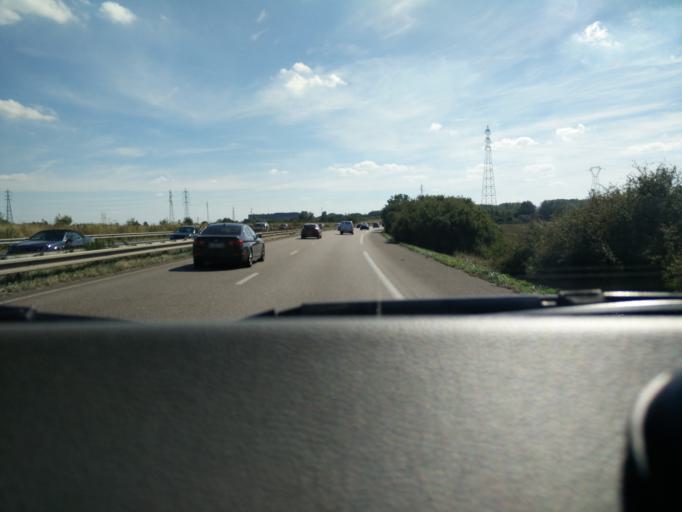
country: FR
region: Lorraine
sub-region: Departement de la Moselle
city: Bertrange
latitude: 49.2989
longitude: 6.1834
